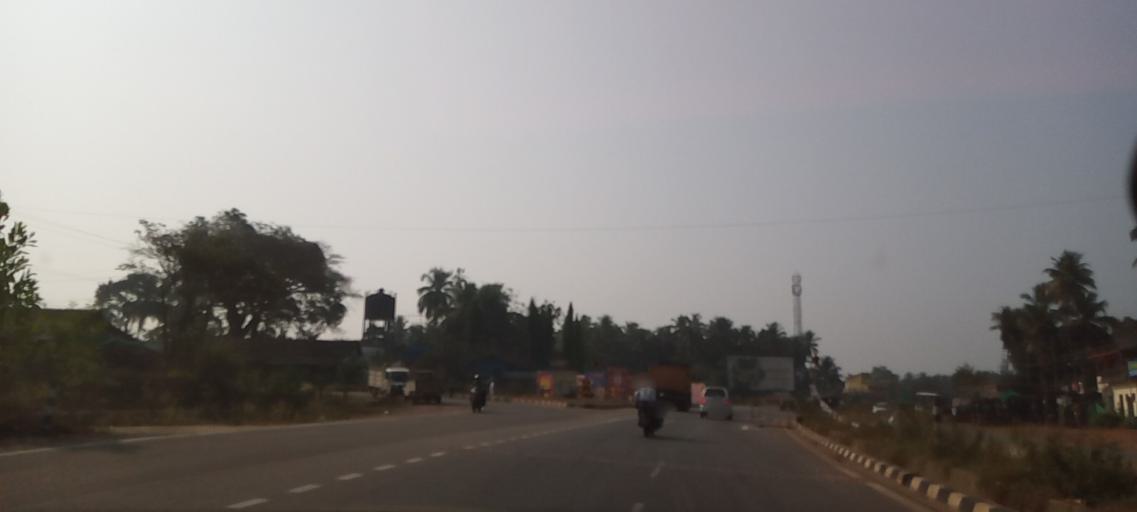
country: IN
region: Karnataka
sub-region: Udupi
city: Coondapoor
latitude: 13.6567
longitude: 74.7088
